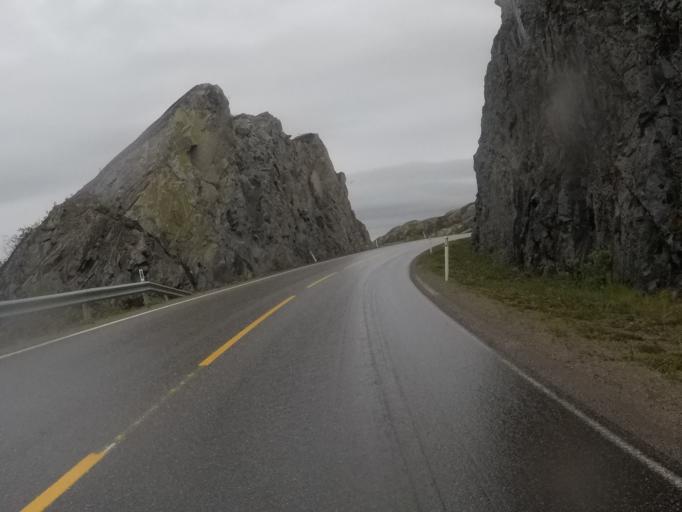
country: NO
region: Finnmark Fylke
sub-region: Nesseby
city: Vuonnabahta
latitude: 70.0787
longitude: 28.7823
